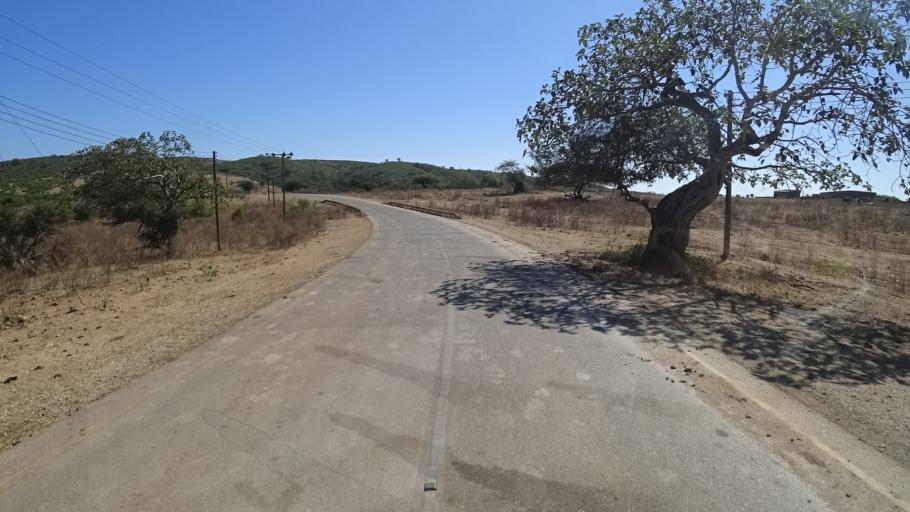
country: YE
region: Al Mahrah
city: Hawf
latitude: 16.7539
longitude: 53.3405
